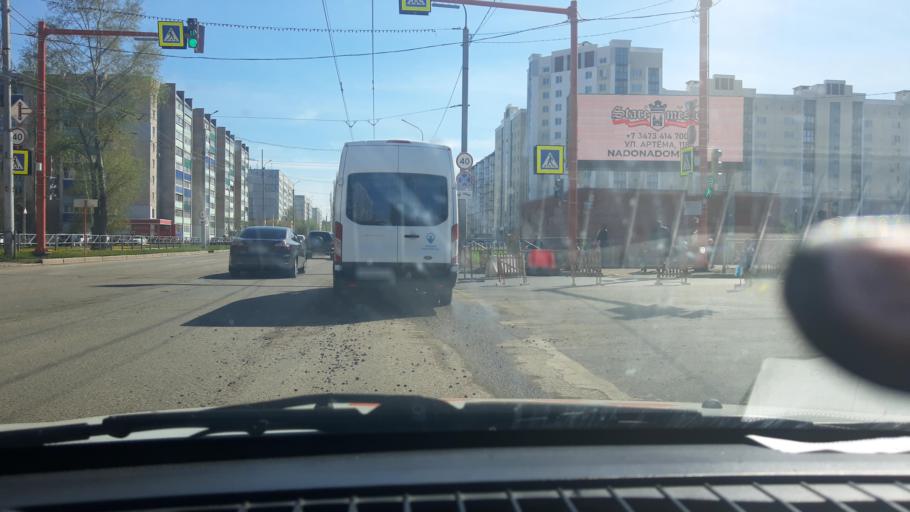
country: RU
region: Bashkortostan
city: Sterlitamak
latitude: 53.6303
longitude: 55.9037
